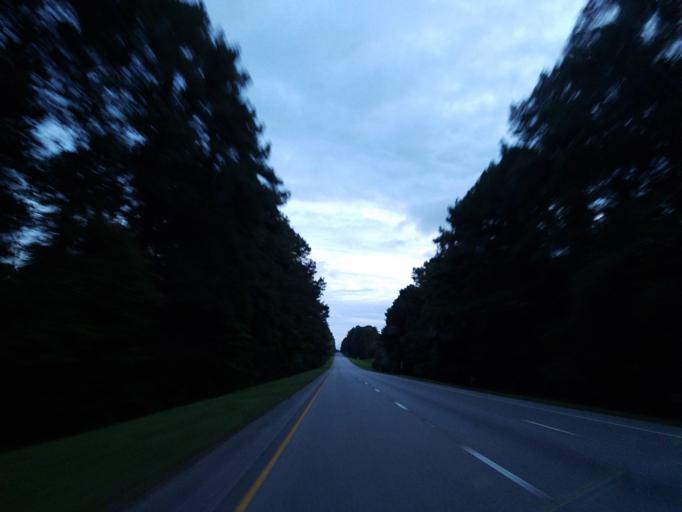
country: US
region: Mississippi
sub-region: Clarke County
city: Stonewall
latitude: 32.1593
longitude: -88.8681
